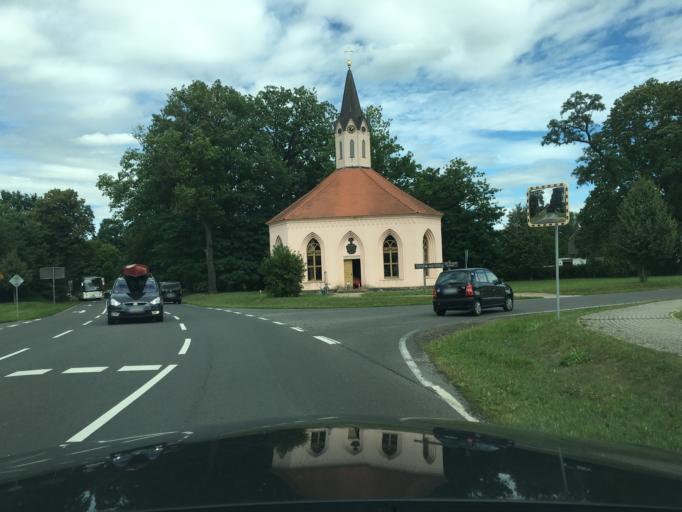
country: DE
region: Brandenburg
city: Gransee
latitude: 53.0794
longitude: 13.1850
